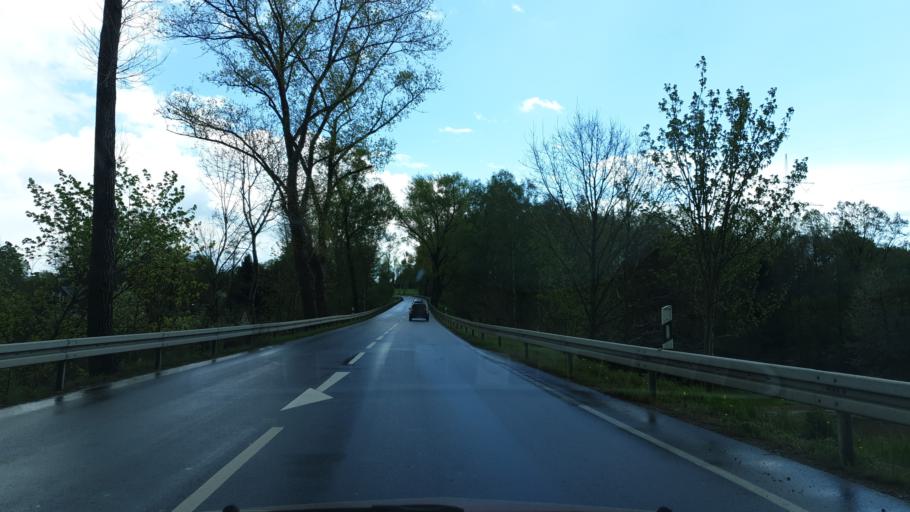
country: DE
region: Saxony
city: Neukirchen
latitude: 50.8083
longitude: 12.8215
